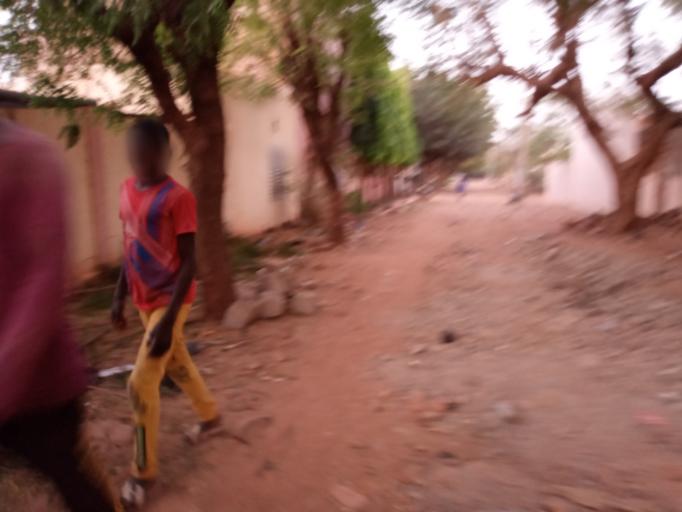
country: ML
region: Bamako
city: Bamako
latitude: 12.5814
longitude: -7.9512
